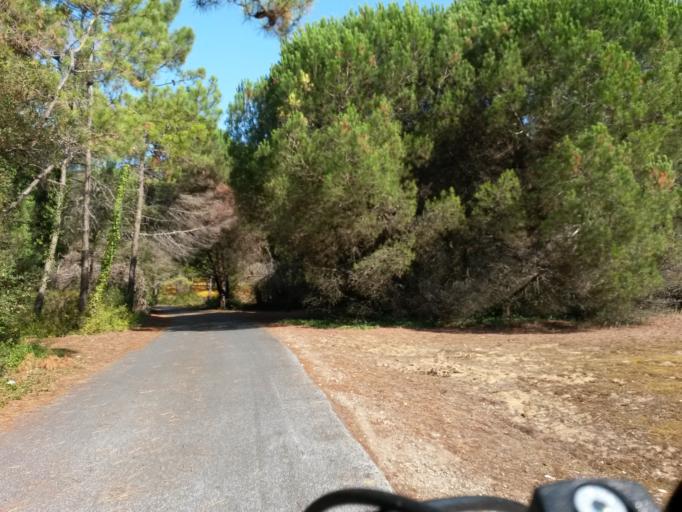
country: FR
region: Poitou-Charentes
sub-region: Departement de la Charente-Maritime
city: Le Bois-Plage-en-Re
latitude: 46.1772
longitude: -1.3704
